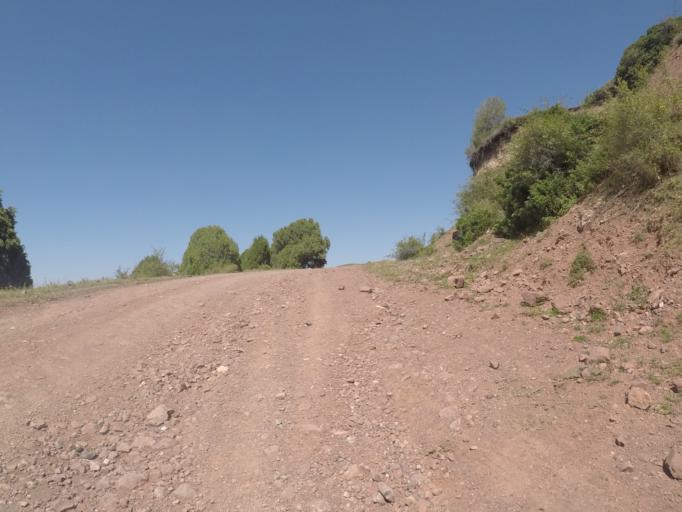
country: KG
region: Chuy
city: Bishkek
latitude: 42.6468
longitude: 74.5665
